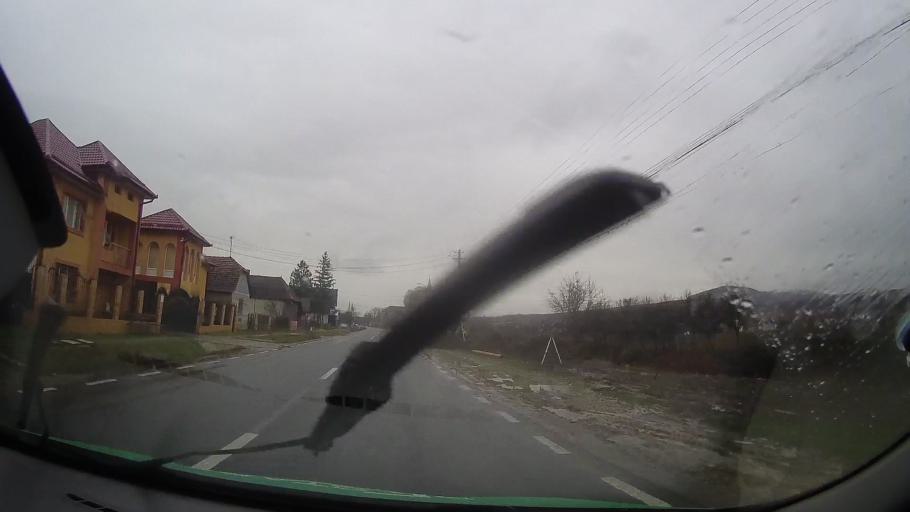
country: RO
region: Bistrita-Nasaud
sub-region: Comuna Galatii Bistritei
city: Galatii Bistritei
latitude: 46.9733
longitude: 24.4331
